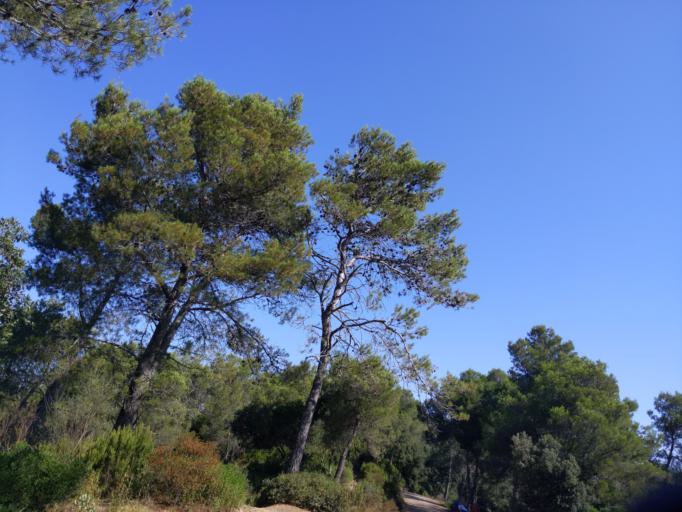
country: ES
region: Catalonia
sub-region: Provincia de Barcelona
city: Cerdanyola del Valles
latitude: 41.4539
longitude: 2.1372
